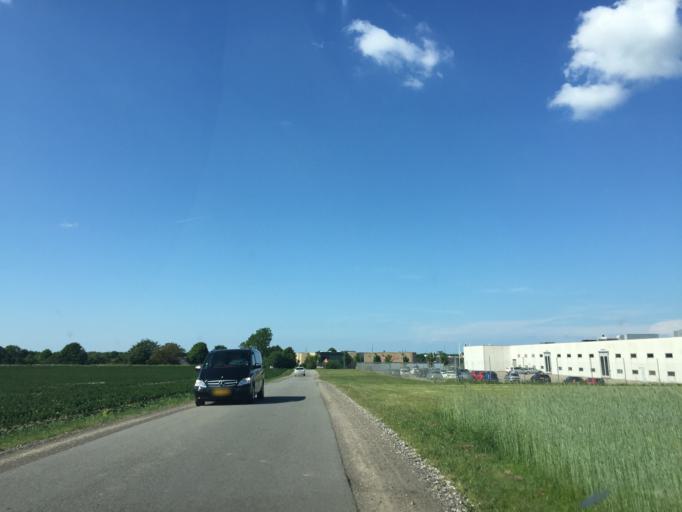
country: DK
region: South Denmark
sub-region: Odense Kommune
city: Hojby
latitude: 55.3428
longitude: 10.3970
